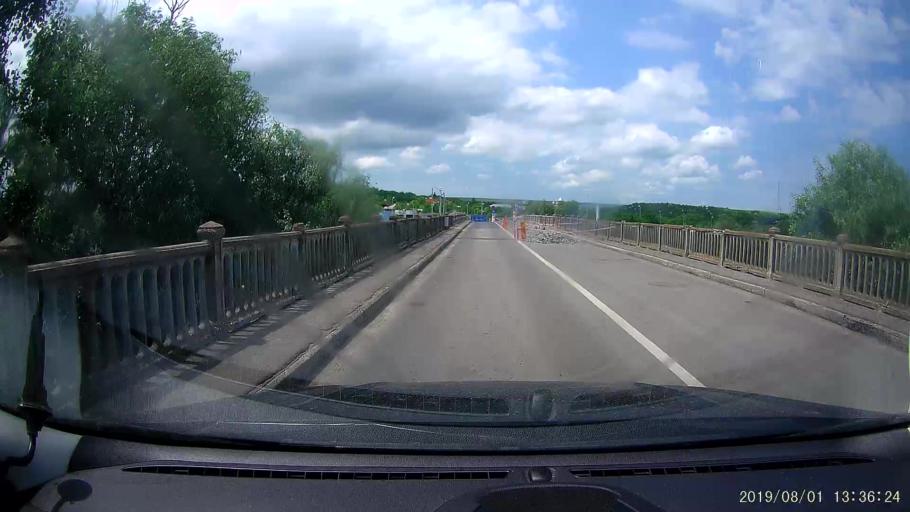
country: RO
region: Galati
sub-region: Comuna Oancea
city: Oancea
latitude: 45.9173
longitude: 28.1210
